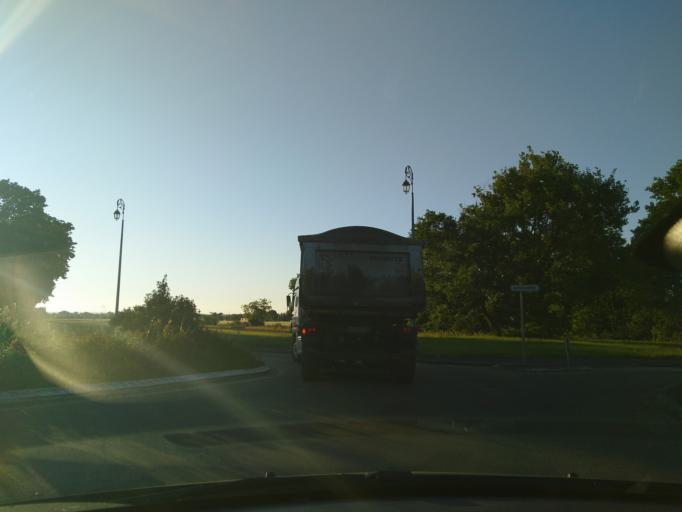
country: FR
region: Midi-Pyrenees
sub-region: Departement de la Haute-Garonne
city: Merville
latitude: 43.7181
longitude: 1.3055
